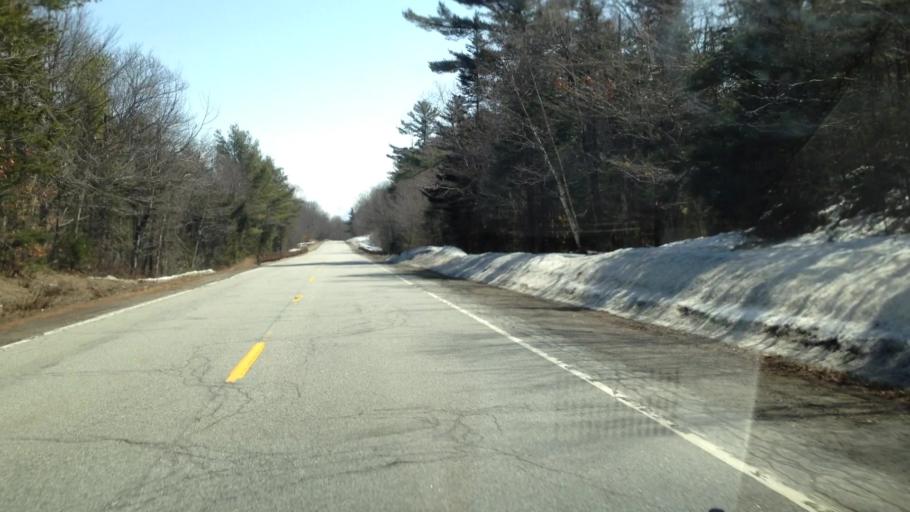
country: US
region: New Hampshire
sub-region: Sullivan County
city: Springfield
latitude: 43.4921
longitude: -71.9876
